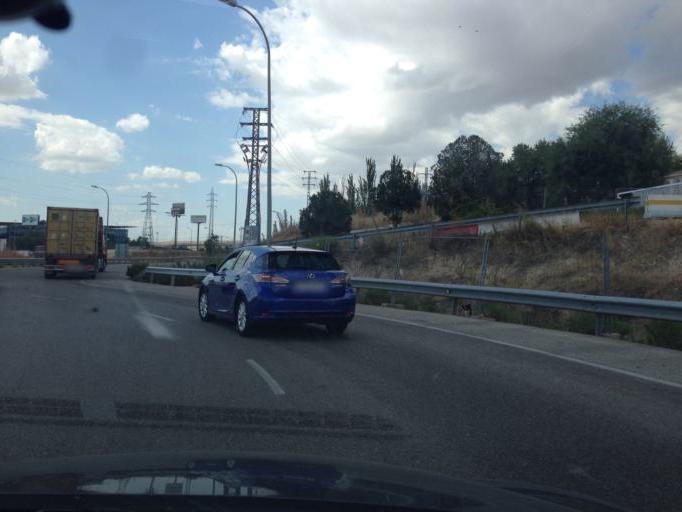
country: ES
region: Madrid
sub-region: Provincia de Madrid
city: San Fernando de Henares
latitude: 40.4558
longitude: -3.5112
